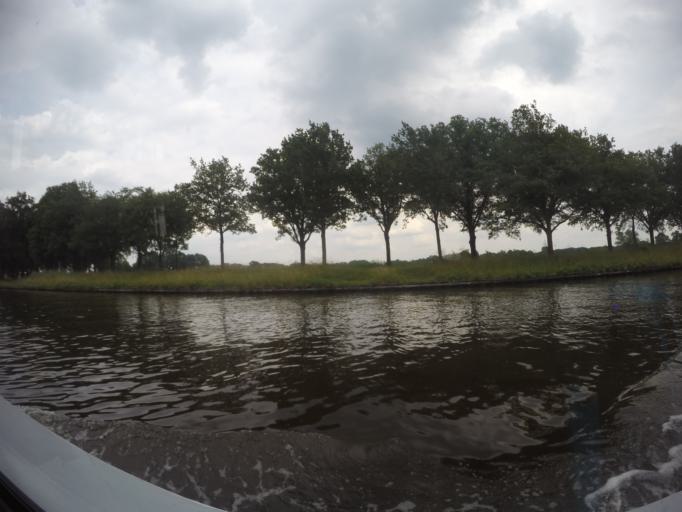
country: NL
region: Overijssel
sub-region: Gemeente Hof van Twente
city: Delden
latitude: 52.2759
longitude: 6.6434
